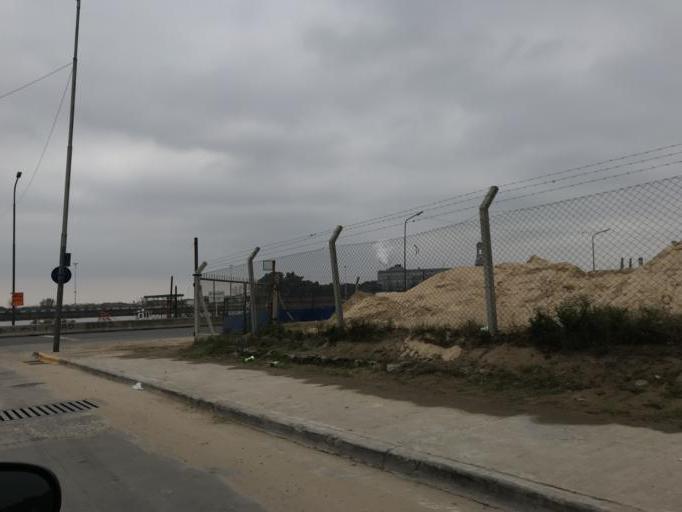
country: AR
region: Buenos Aires F.D.
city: Retiro
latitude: -34.5732
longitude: -58.3920
